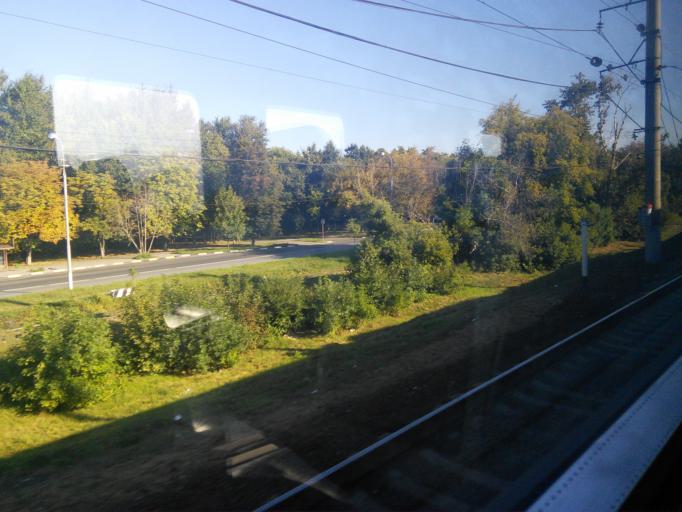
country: RU
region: Moskovskaya
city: Kur'yanovo
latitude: 55.6523
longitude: 37.7043
